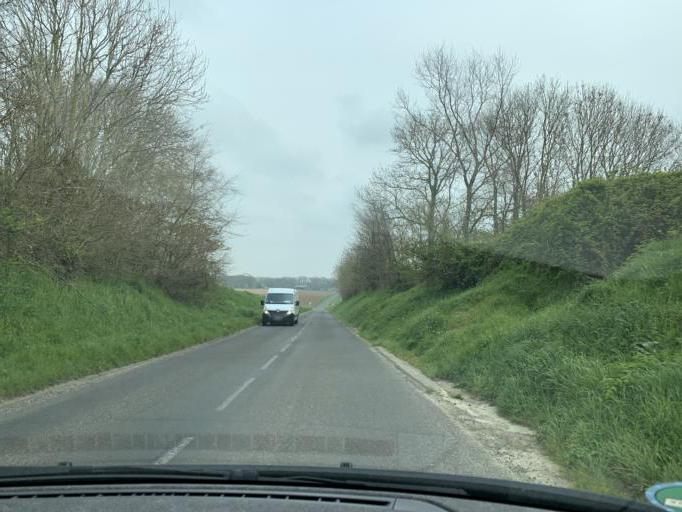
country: FR
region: Haute-Normandie
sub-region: Departement de la Seine-Maritime
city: Saint-Valery-en-Caux
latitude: 49.8542
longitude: 0.7785
